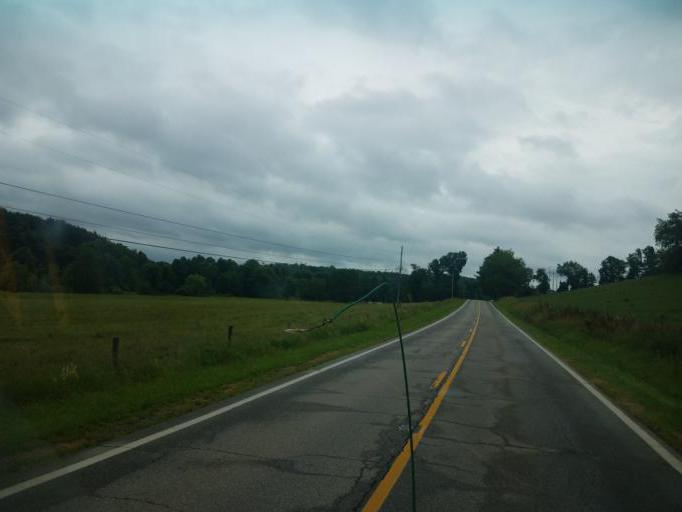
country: US
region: Ohio
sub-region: Stark County
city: Minerva
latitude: 40.6614
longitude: -81.0451
